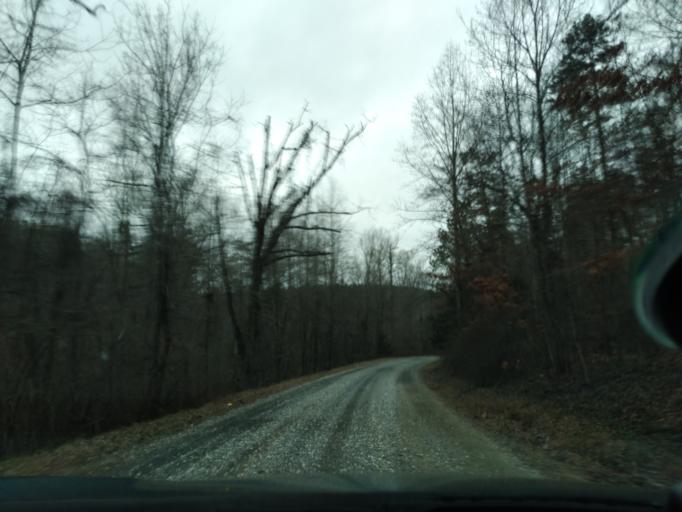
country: US
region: Virginia
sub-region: Buckingham County
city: Buckingham
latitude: 37.4253
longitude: -78.6578
